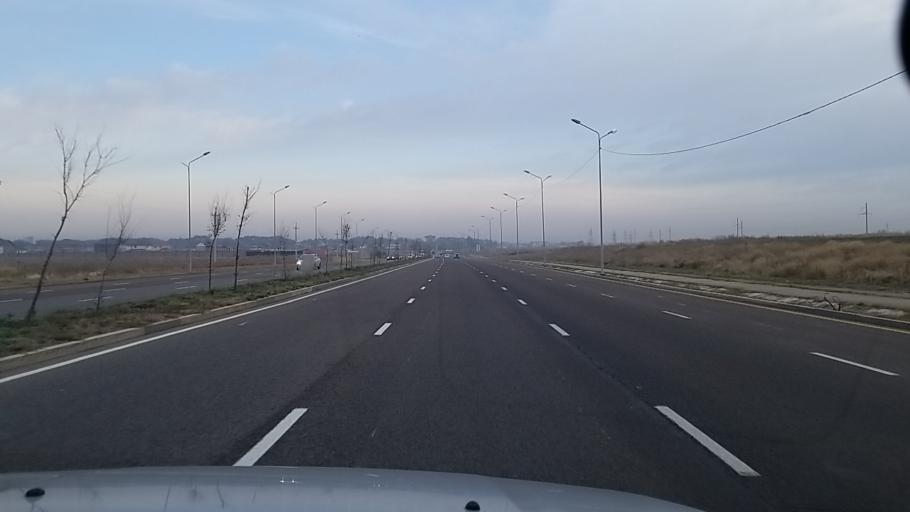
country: KZ
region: Almaty Oblysy
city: Burunday
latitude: 43.3445
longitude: 76.8339
